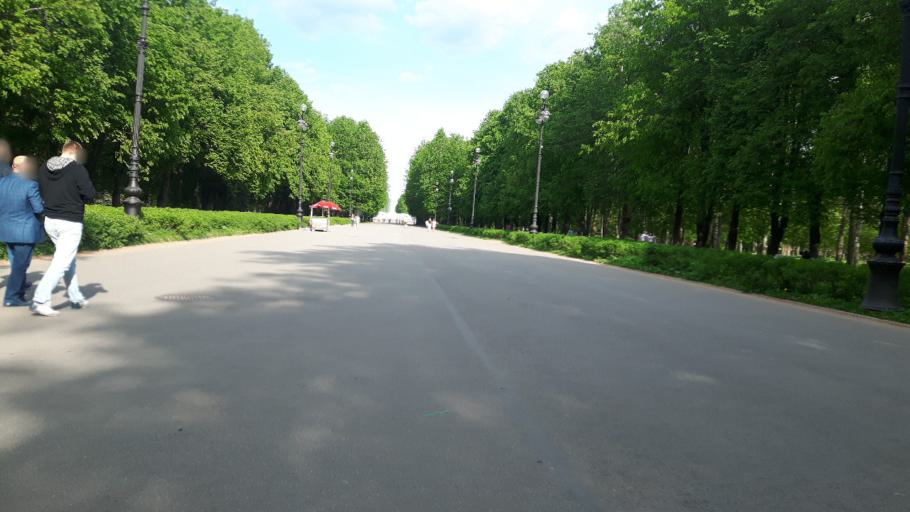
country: RU
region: St.-Petersburg
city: Staraya Derevnya
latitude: 59.9723
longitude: 30.2341
